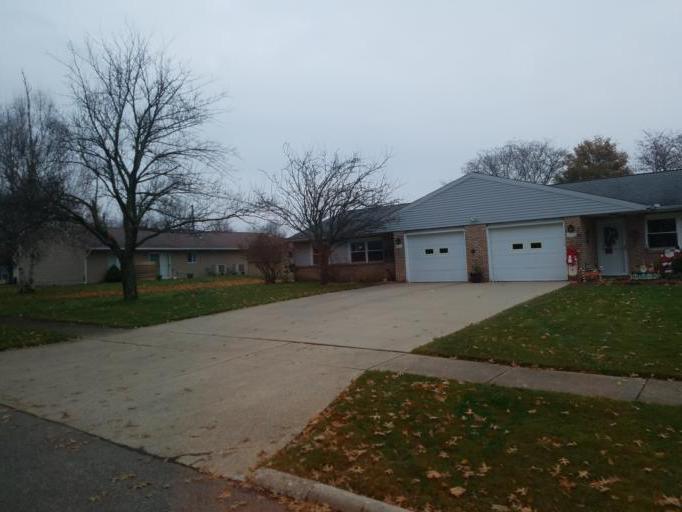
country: US
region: Ohio
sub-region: Richland County
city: Lexington
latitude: 40.7100
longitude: -82.5389
